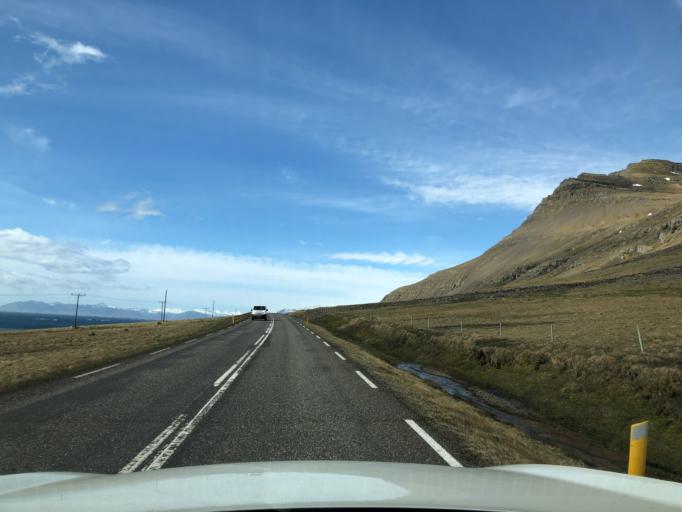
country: IS
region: East
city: Reydarfjoerdur
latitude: 64.7124
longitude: -14.0764
